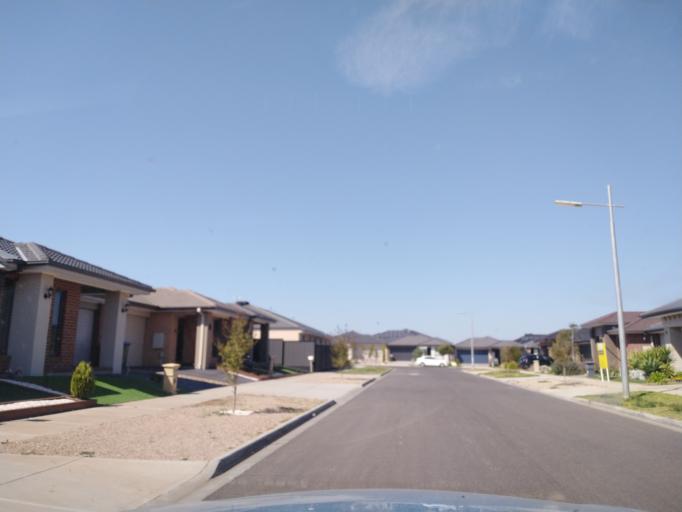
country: AU
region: Victoria
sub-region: Wyndham
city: Williams Landing
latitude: -37.8425
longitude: 144.7406
